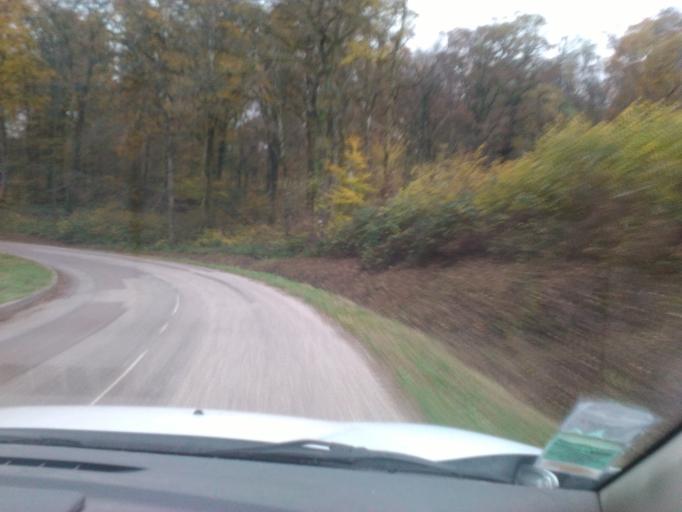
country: FR
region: Lorraine
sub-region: Departement des Vosges
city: Darnieulles
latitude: 48.2407
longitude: 6.2821
